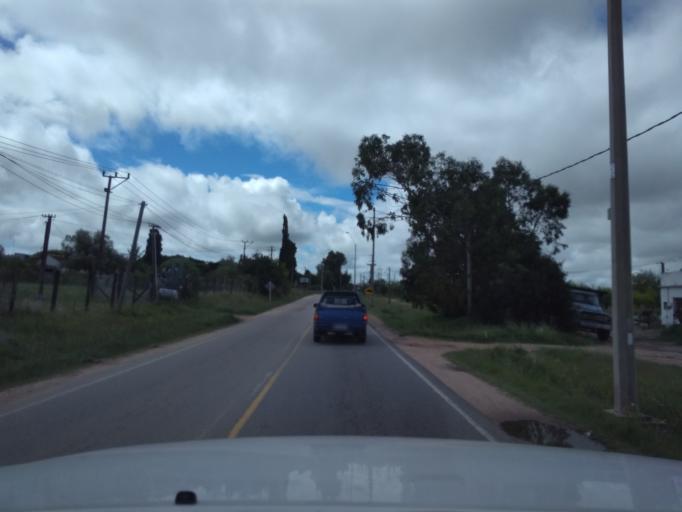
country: UY
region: Canelones
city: Pando
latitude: -34.6966
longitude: -55.9673
